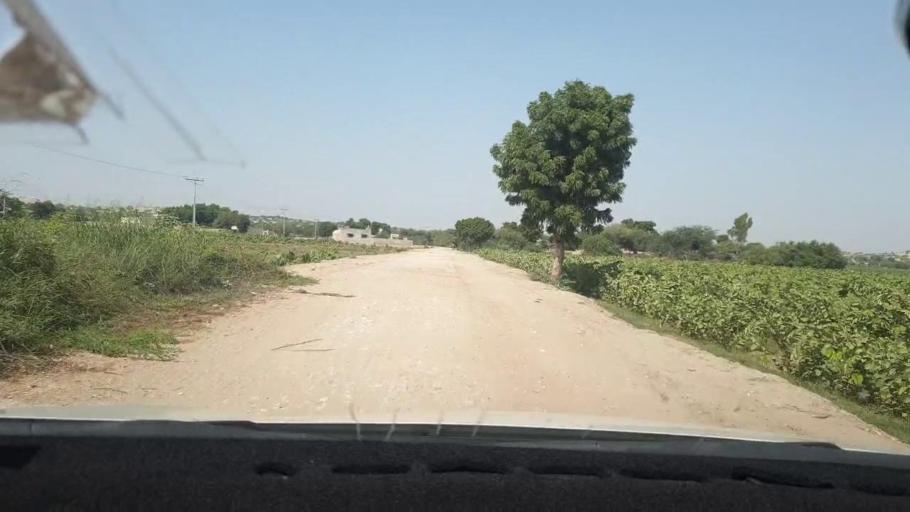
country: PK
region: Sindh
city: Tando Mittha Khan
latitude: 25.8727
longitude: 69.3879
